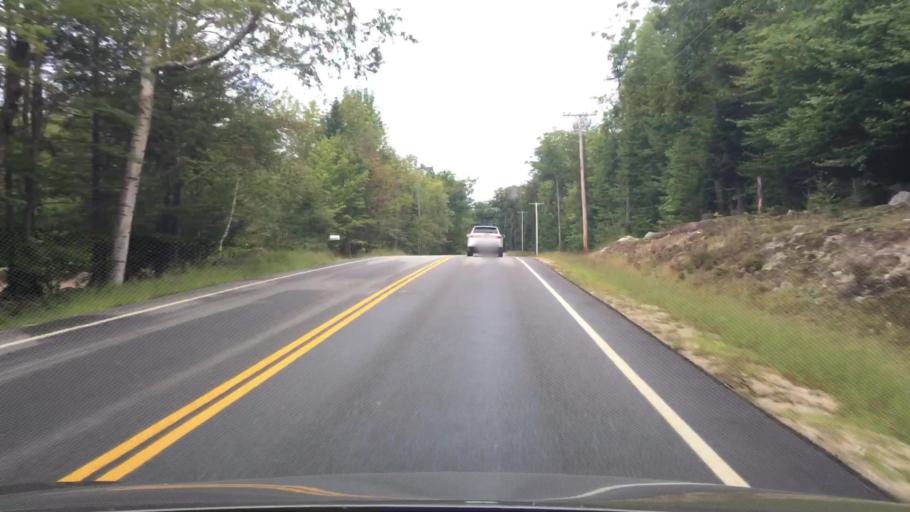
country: US
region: Maine
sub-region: Oxford County
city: Hartford
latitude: 44.3592
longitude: -70.3090
